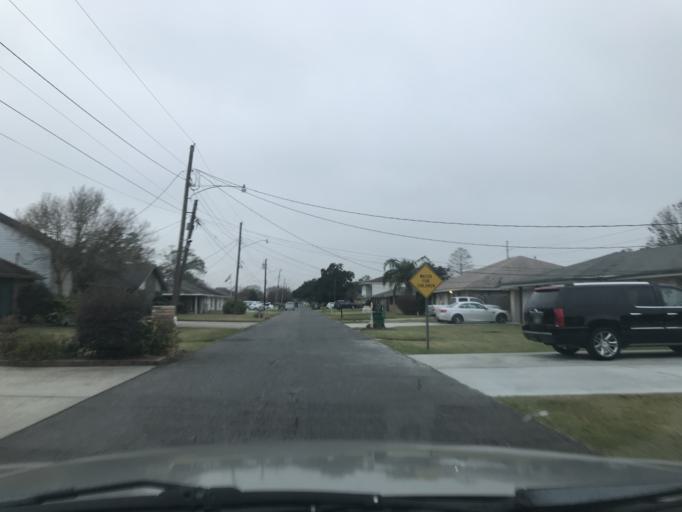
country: US
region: Louisiana
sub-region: Jefferson Parish
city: Woodmere
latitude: 29.8672
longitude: -90.0913
